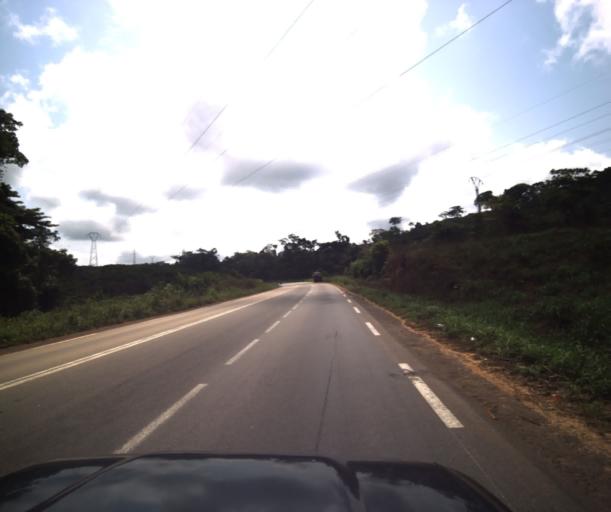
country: CM
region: Centre
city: Eseka
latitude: 3.8728
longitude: 10.8281
